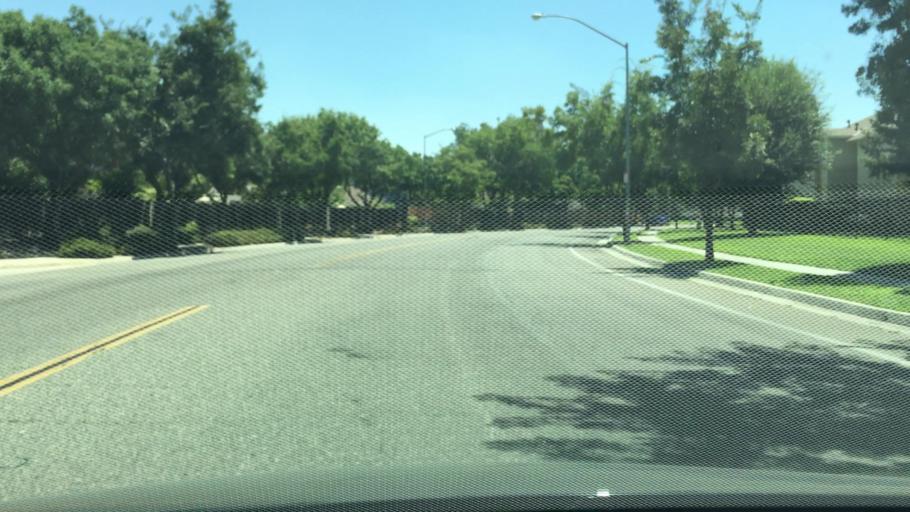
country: US
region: California
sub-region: Fresno County
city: Clovis
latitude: 36.8426
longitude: -119.7461
